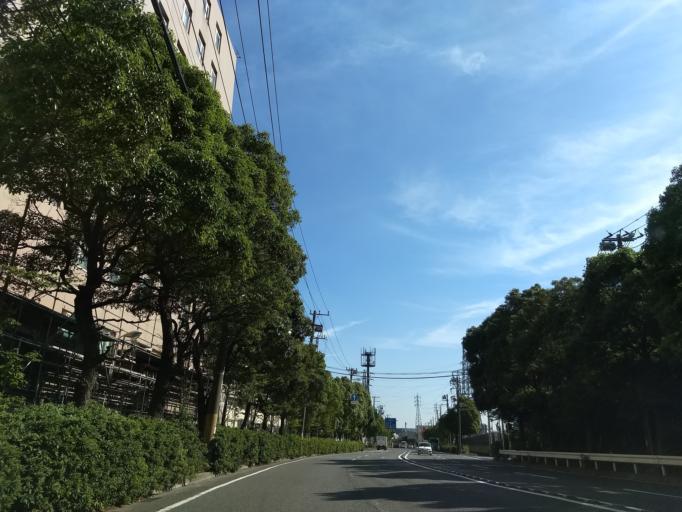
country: JP
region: Kanagawa
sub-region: Kawasaki-shi
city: Kawasaki
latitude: 35.5279
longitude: 139.7491
